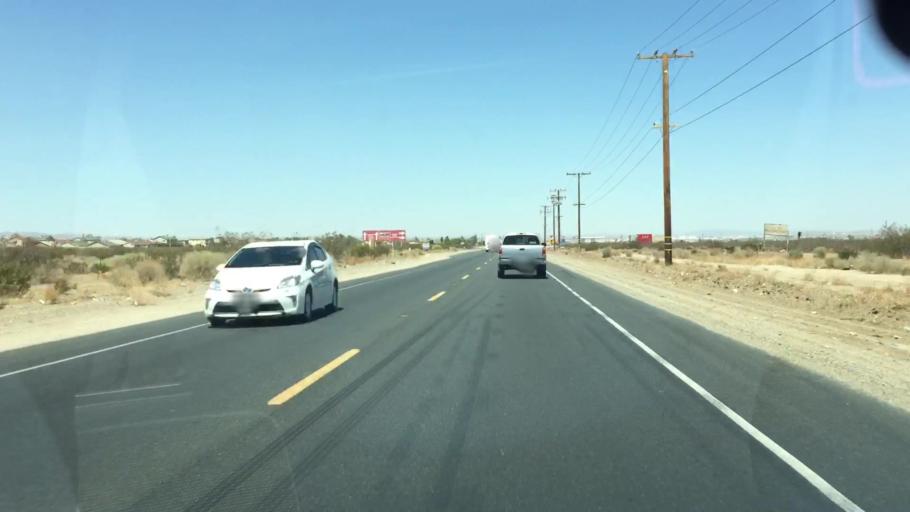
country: US
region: California
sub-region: San Bernardino County
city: Mountain View Acres
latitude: 34.4871
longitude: -117.3995
